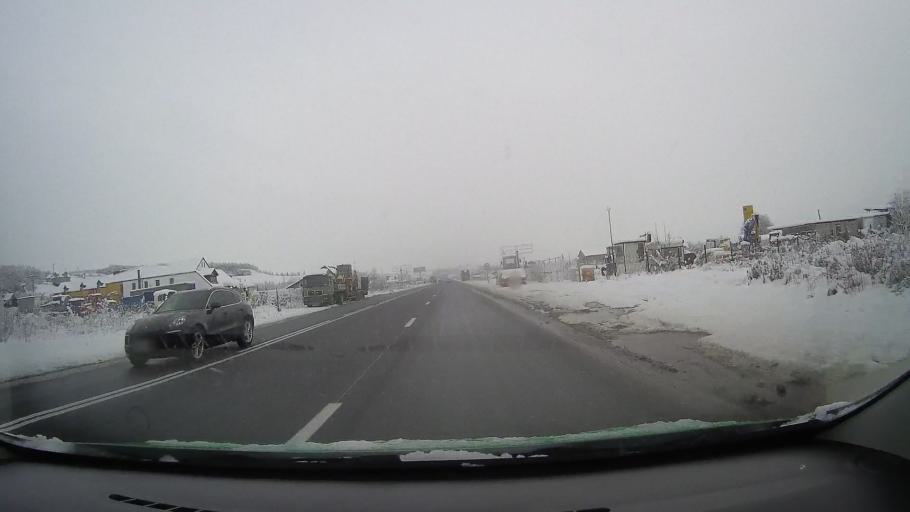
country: RO
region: Sibiu
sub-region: Comuna Cristian
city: Cristian
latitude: 45.7881
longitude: 24.0397
